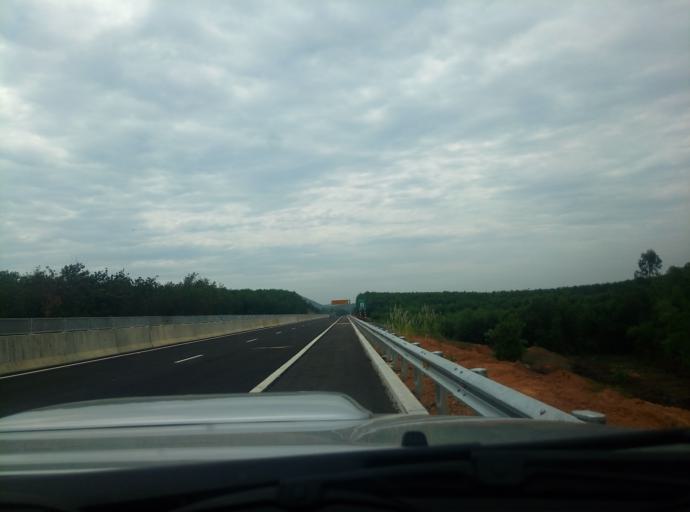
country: VN
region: Quang Nam
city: Nui Thanh
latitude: 15.4504
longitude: 108.5775
